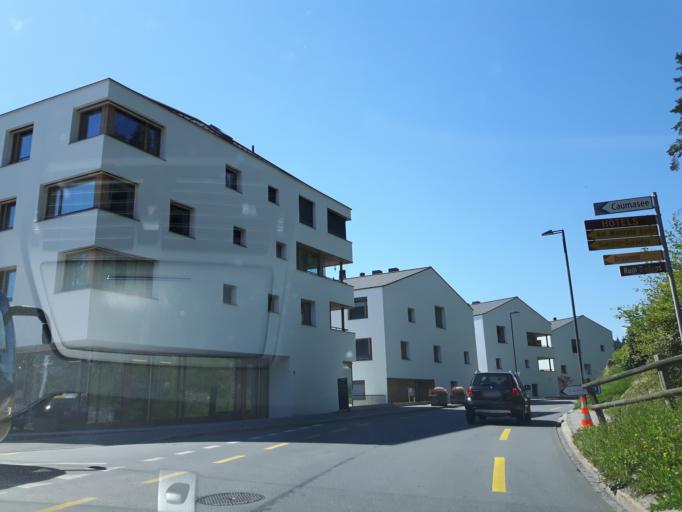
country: CH
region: Grisons
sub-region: Imboden District
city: Flims
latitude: 46.8260
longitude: 9.2882
